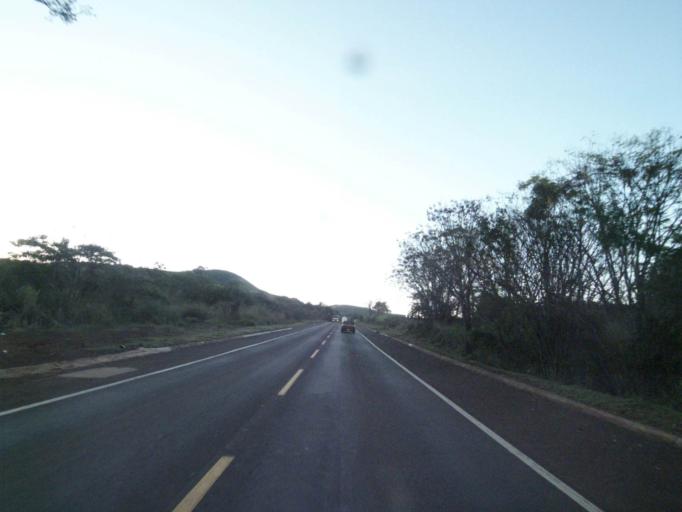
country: BR
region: Parana
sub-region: Londrina
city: Londrina
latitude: -23.5507
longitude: -51.1213
